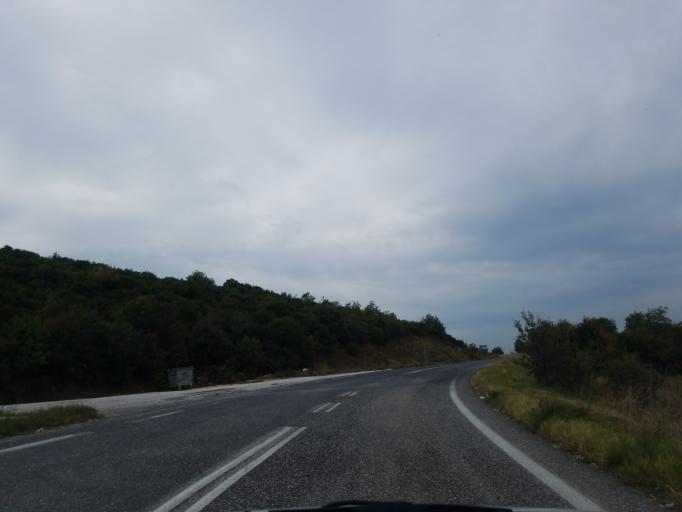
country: GR
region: Central Greece
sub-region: Nomos Fthiotidos
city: Domokos
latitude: 39.1449
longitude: 22.3130
